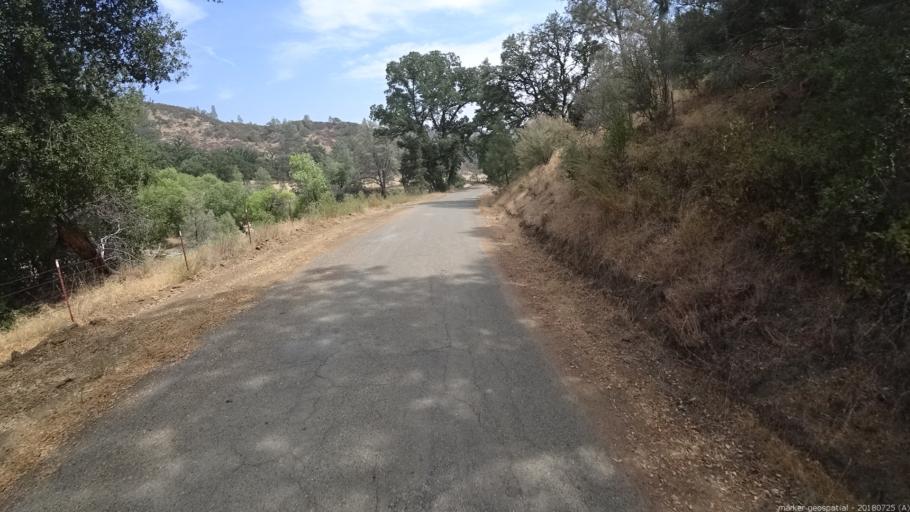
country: US
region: California
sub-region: Fresno County
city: Coalinga
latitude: 36.2251
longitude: -120.7075
